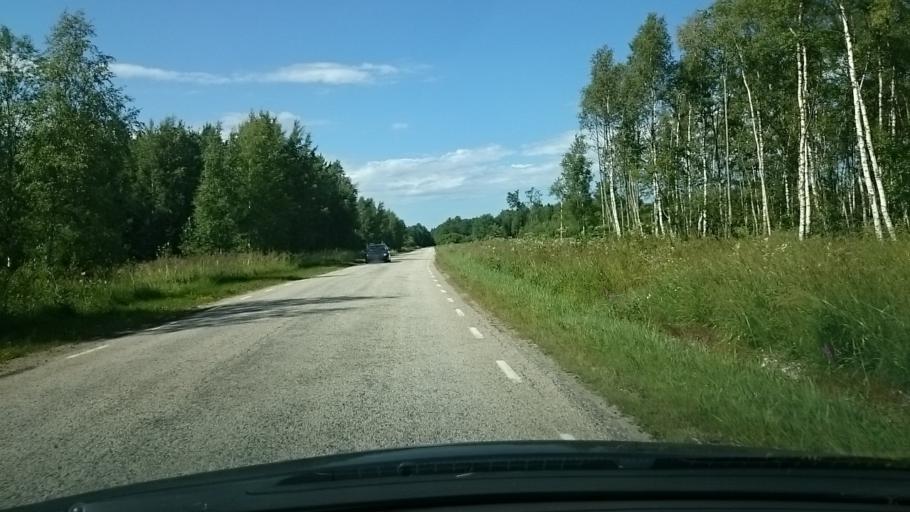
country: EE
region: Laeaene
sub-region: Haapsalu linn
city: Haapsalu
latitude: 59.0891
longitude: 23.5492
